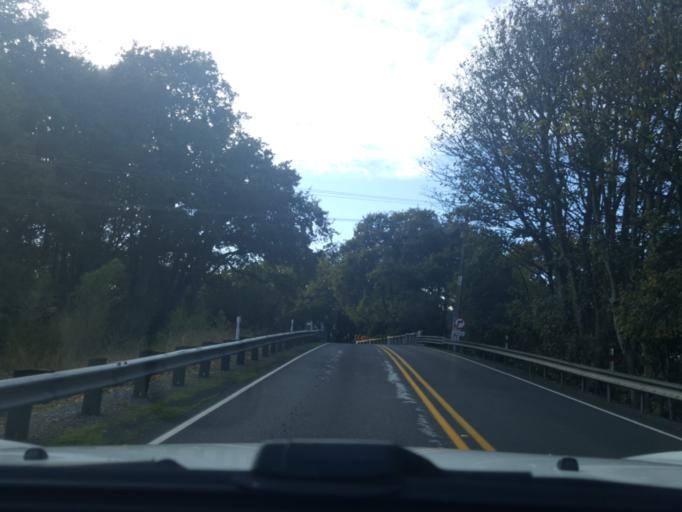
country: NZ
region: Waikato
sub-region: Waipa District
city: Cambridge
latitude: -37.6450
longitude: 175.5557
